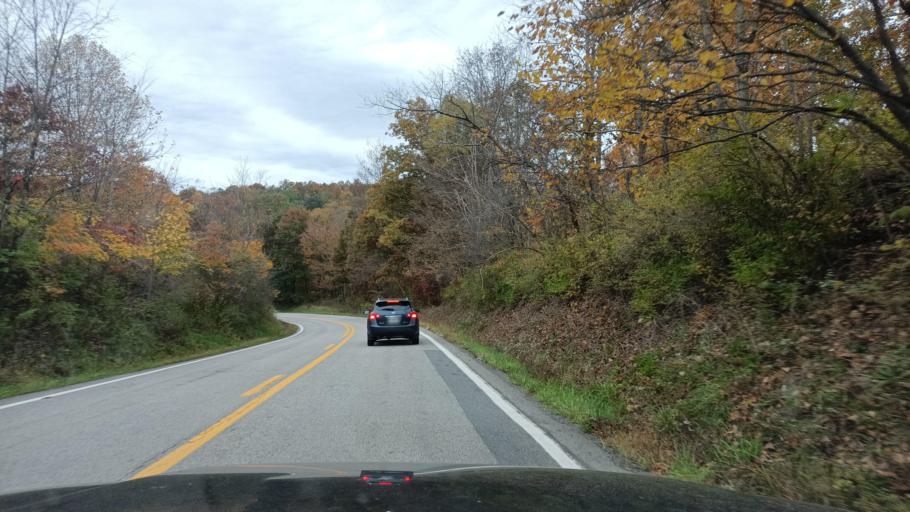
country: US
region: West Virginia
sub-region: Taylor County
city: Grafton
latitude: 39.3437
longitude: -79.9647
